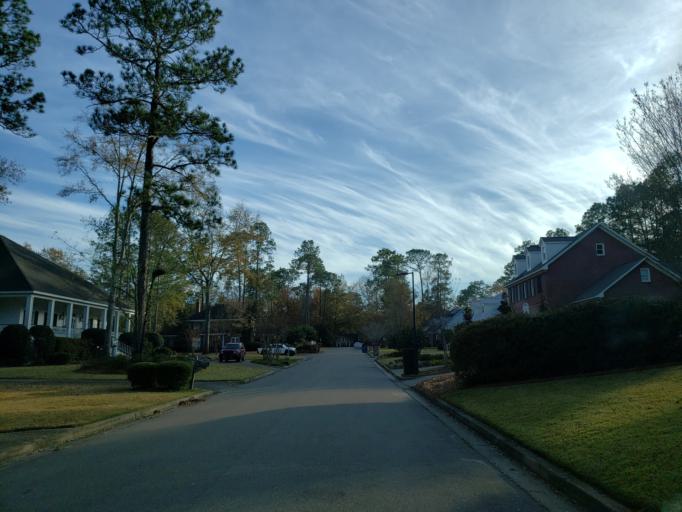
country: US
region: Mississippi
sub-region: Lamar County
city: West Hattiesburg
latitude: 31.3004
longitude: -89.3390
